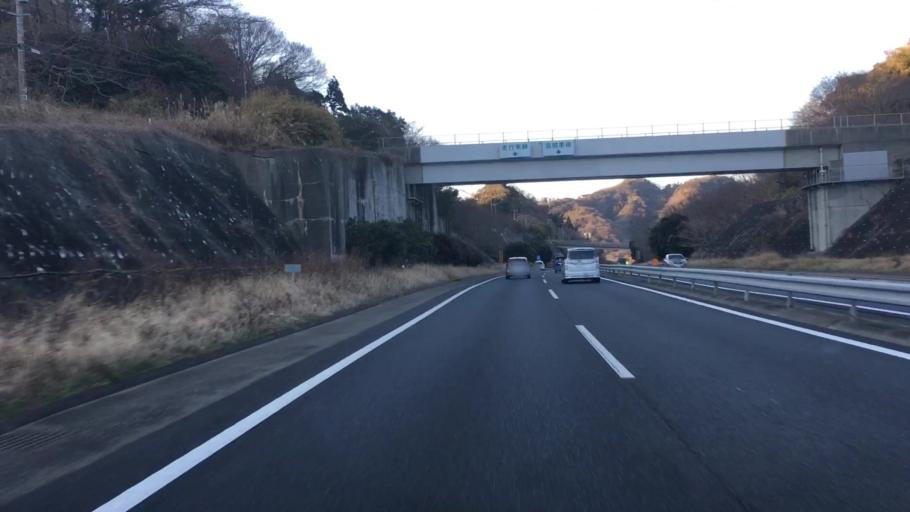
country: JP
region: Kanagawa
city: Yokosuka
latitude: 35.2582
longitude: 139.6347
